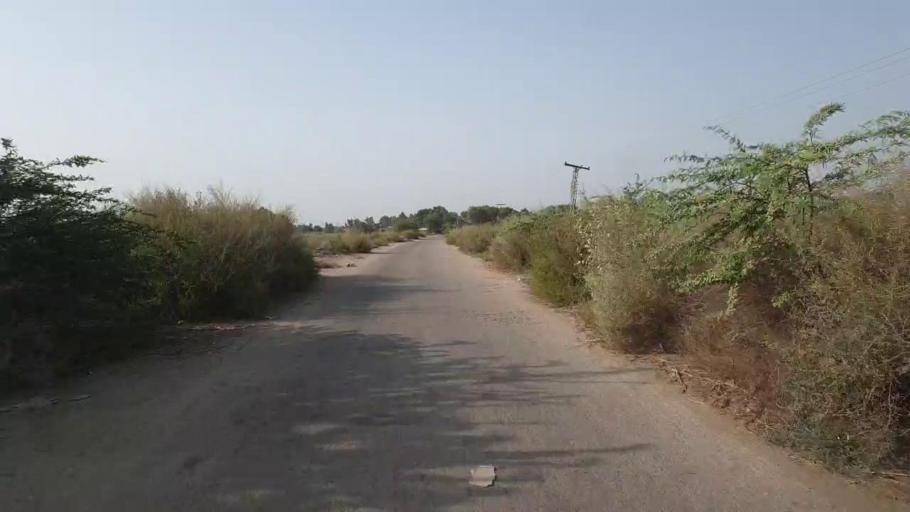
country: PK
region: Sindh
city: Jam Sahib
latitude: 26.4240
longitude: 68.8719
